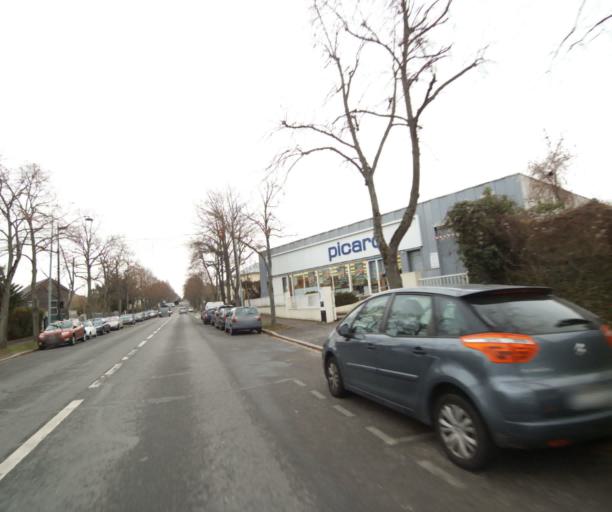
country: FR
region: Ile-de-France
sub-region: Departement des Hauts-de-Seine
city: Rueil-Malmaison
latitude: 48.8639
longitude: 2.1807
